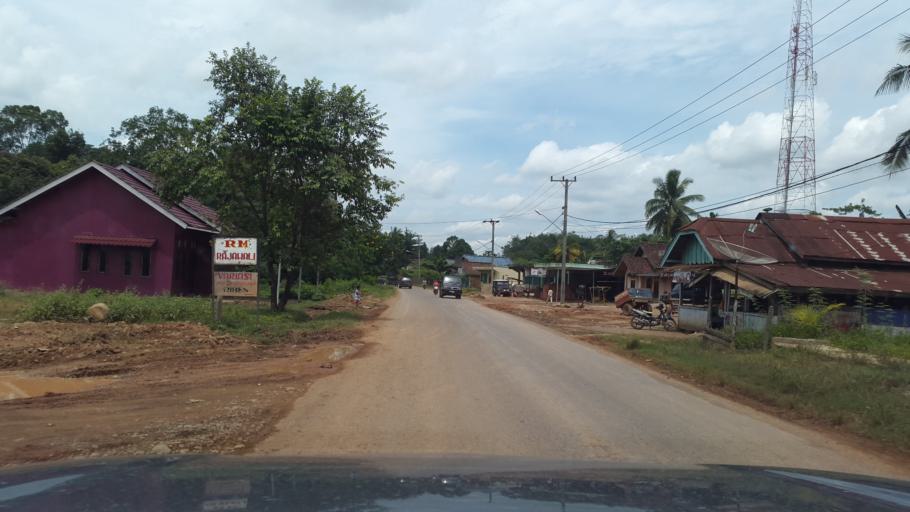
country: ID
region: South Sumatra
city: Gunungmegang Dalam
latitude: -3.3206
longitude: 103.9010
